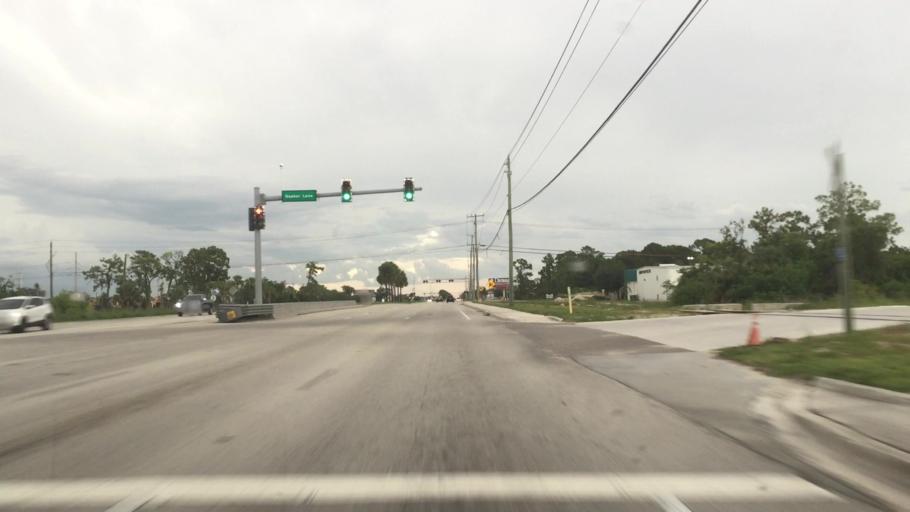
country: US
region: Florida
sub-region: Lee County
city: San Carlos Park
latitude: 26.4926
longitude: -81.8334
